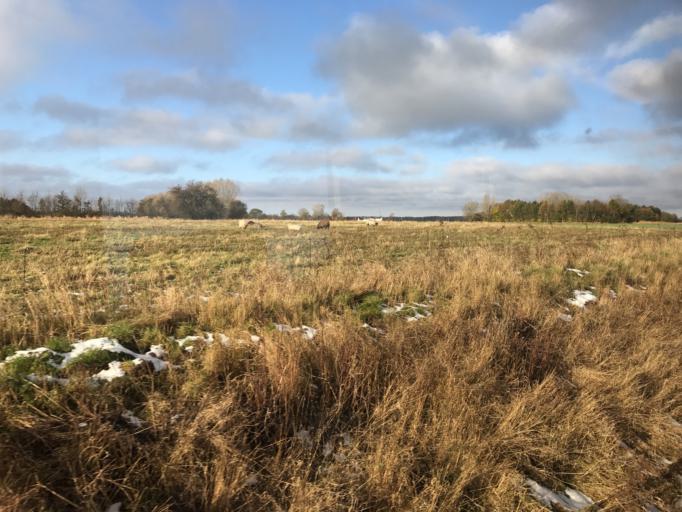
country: DK
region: Zealand
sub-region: Stevns Kommune
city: Harlev
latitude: 55.3561
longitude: 12.2282
